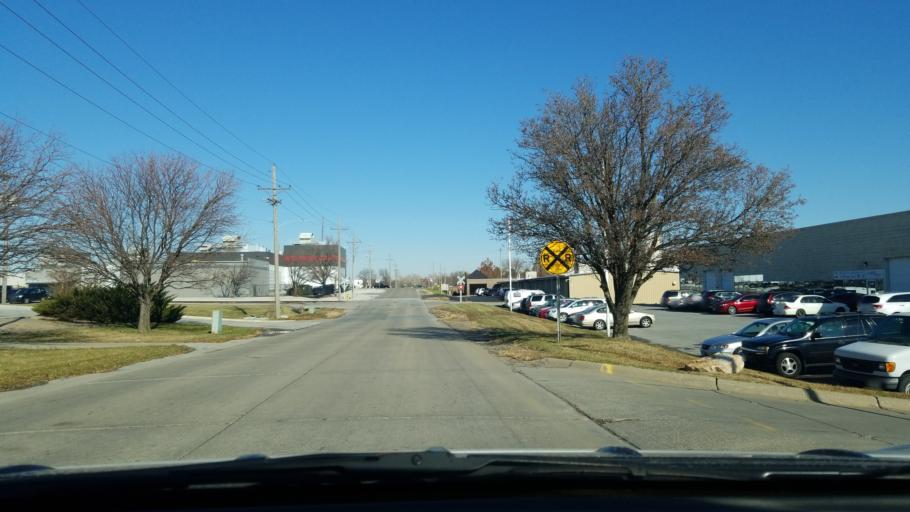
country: US
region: Nebraska
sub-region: Douglas County
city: Ralston
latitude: 41.2144
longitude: -96.0719
